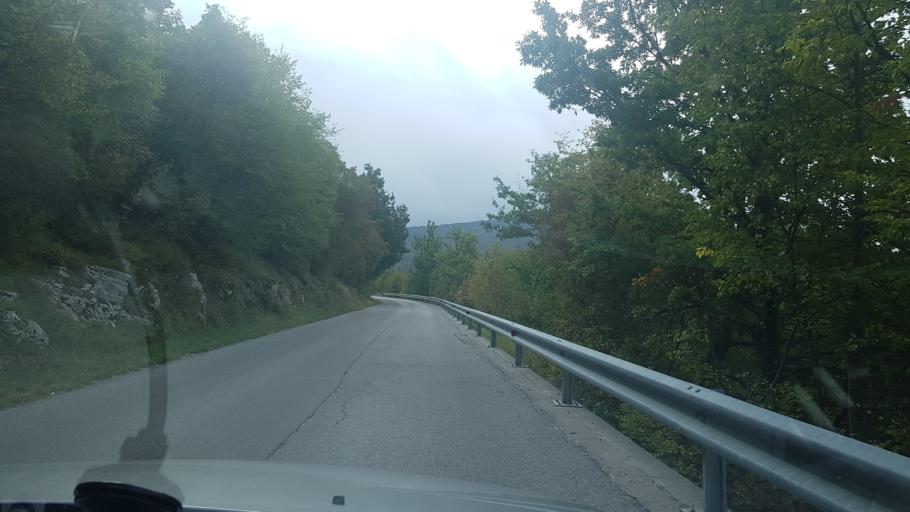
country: SI
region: Hrpelje-Kozina
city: Kozina
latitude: 45.5231
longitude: 13.9557
